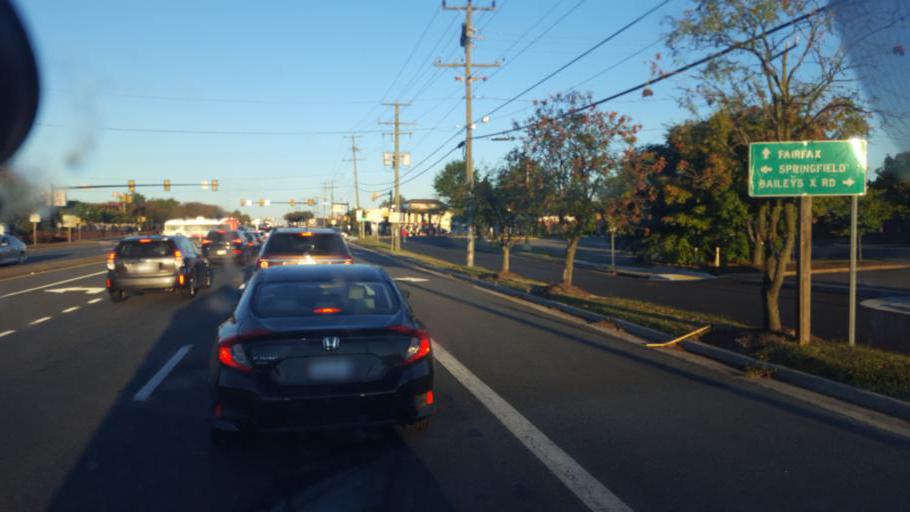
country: US
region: Virginia
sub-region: Fairfax County
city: Annandale
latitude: 38.8293
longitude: -77.1889
